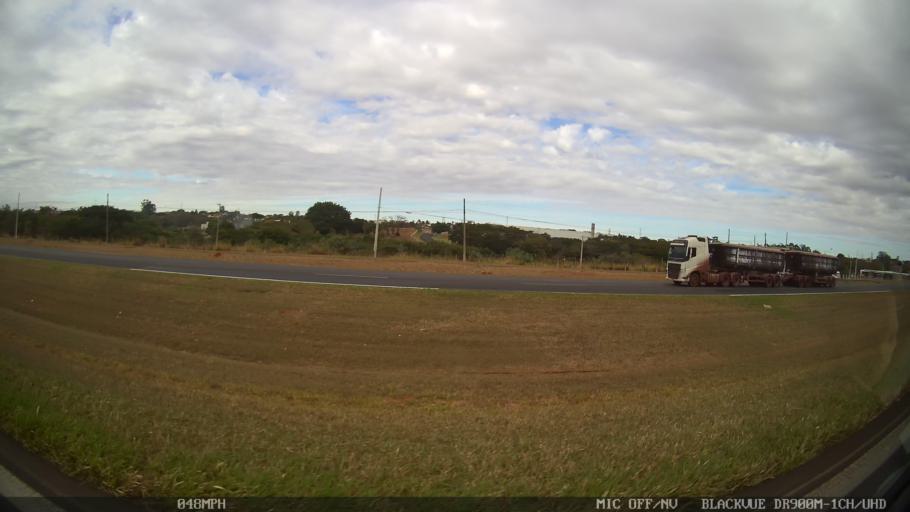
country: BR
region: Sao Paulo
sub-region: Sao Jose Do Rio Preto
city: Sao Jose do Rio Preto
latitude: -20.8131
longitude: -49.4786
